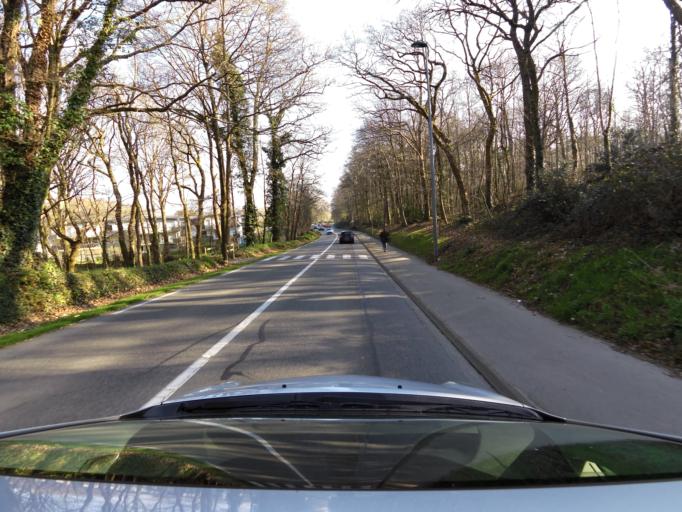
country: FR
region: Brittany
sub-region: Departement du Morbihan
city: Gestel
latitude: 47.7946
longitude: -3.4836
